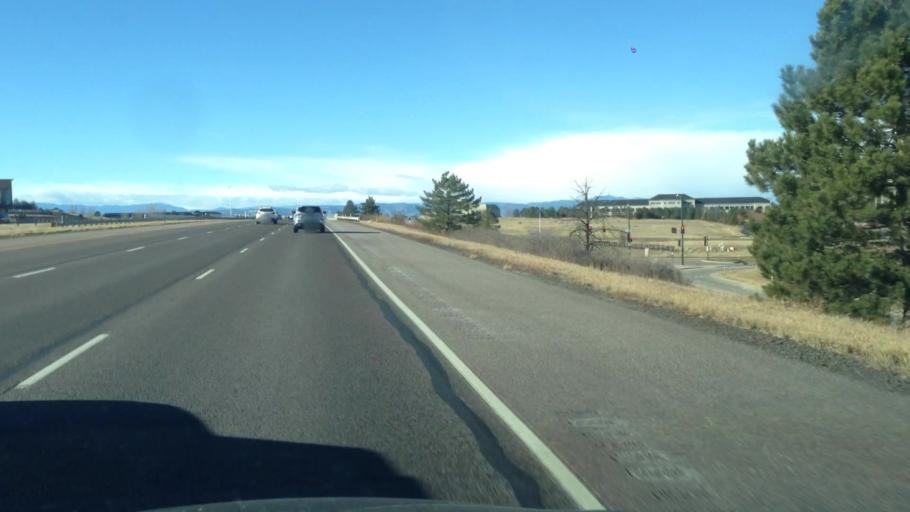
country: US
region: Colorado
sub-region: Douglas County
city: Meridian
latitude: 39.5530
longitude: -104.8372
